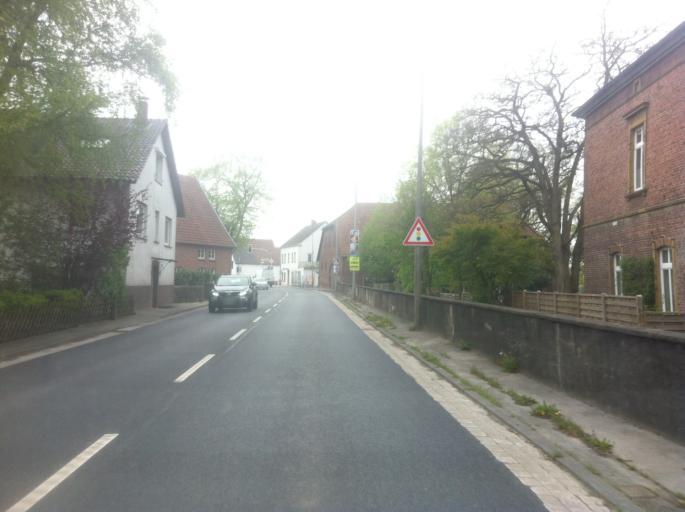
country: DE
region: North Rhine-Westphalia
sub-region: Regierungsbezirk Detmold
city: Lemgo
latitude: 52.0123
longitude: 8.8540
